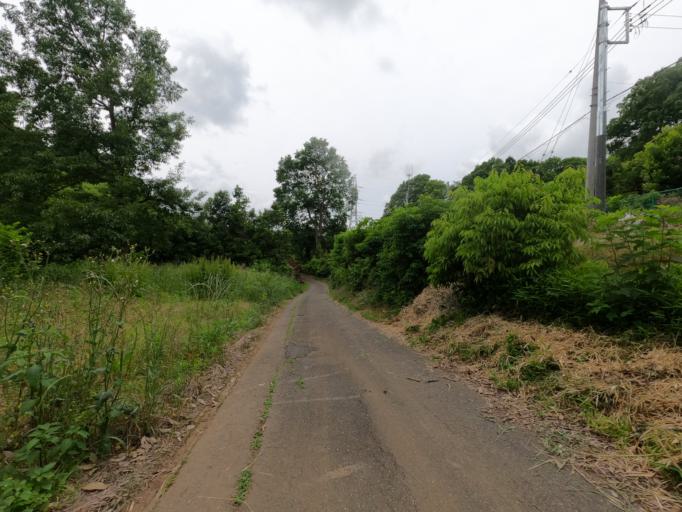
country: JP
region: Ibaraki
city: Moriya
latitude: 35.9544
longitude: 139.9652
